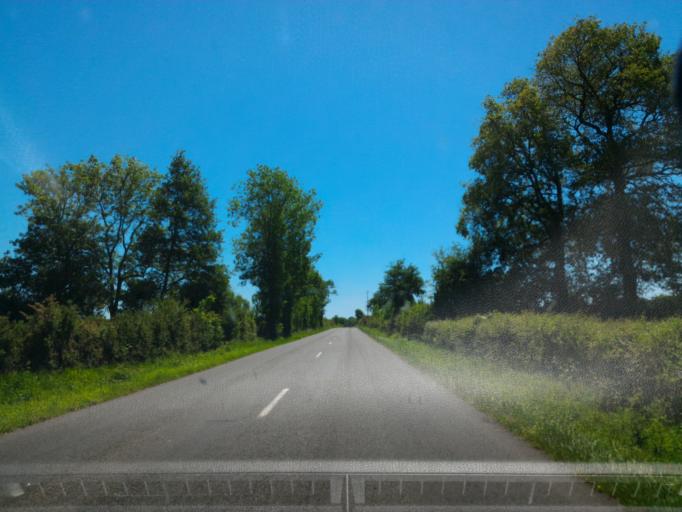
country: FR
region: Poitou-Charentes
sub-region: Departement de la Vienne
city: Availles-Limouzine
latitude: 46.1807
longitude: 0.7267
